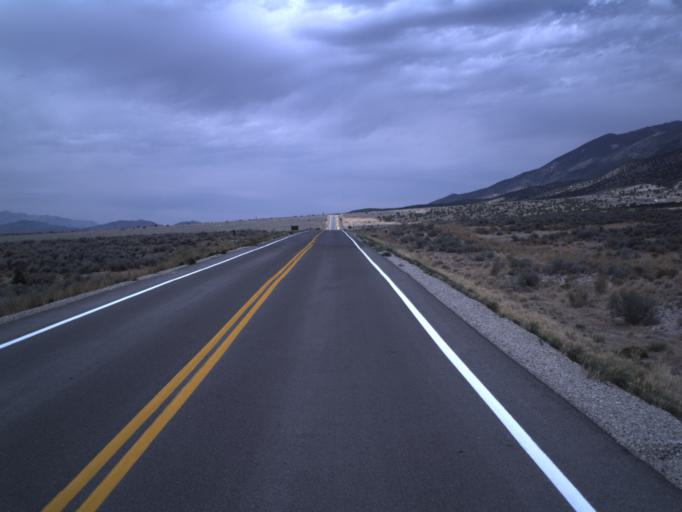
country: US
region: Utah
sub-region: Tooele County
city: Tooele
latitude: 40.3001
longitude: -112.2762
